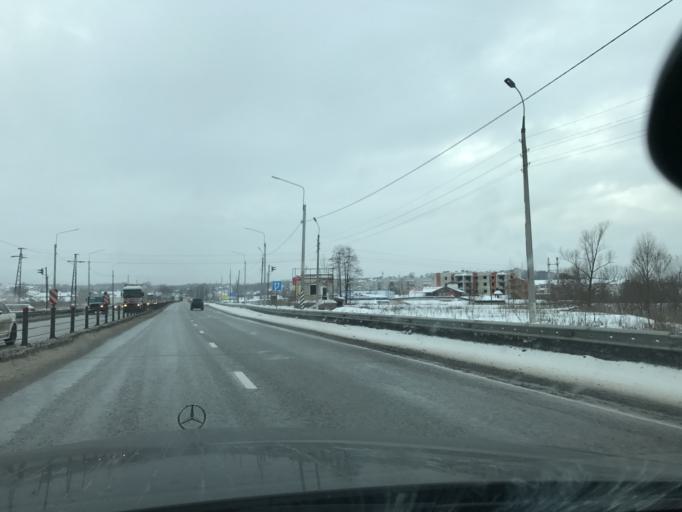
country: RU
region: Vladimir
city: Gorokhovets
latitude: 56.2009
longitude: 42.7121
